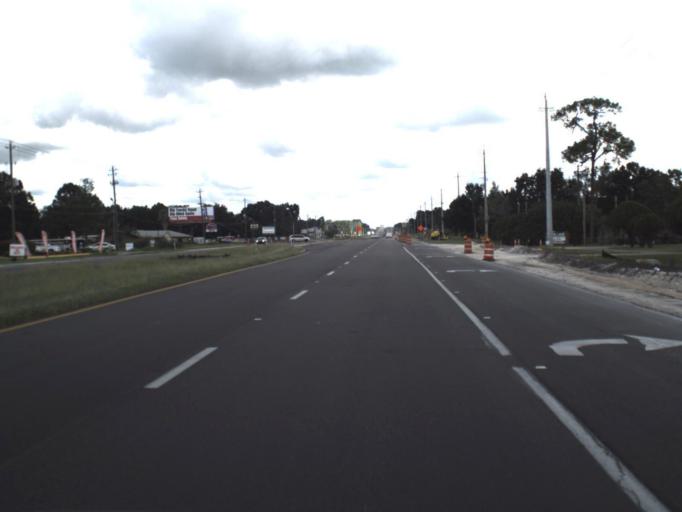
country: US
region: Florida
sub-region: Polk County
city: Gibsonia
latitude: 28.1407
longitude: -81.9735
